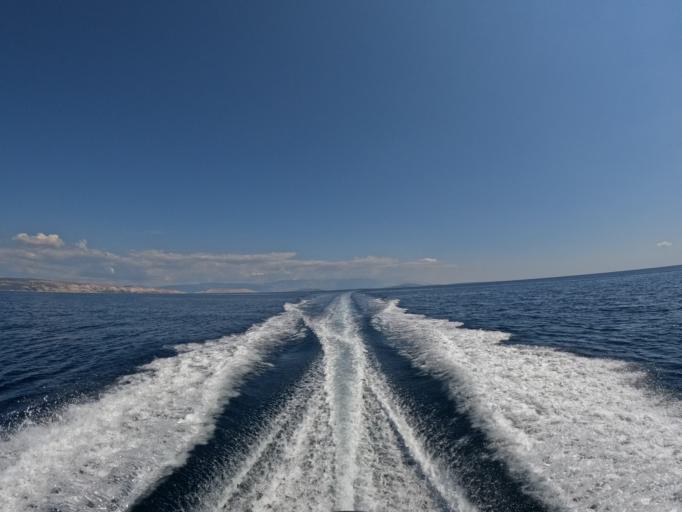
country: HR
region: Primorsko-Goranska
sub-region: Grad Krk
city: Krk
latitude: 44.9328
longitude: 14.5178
